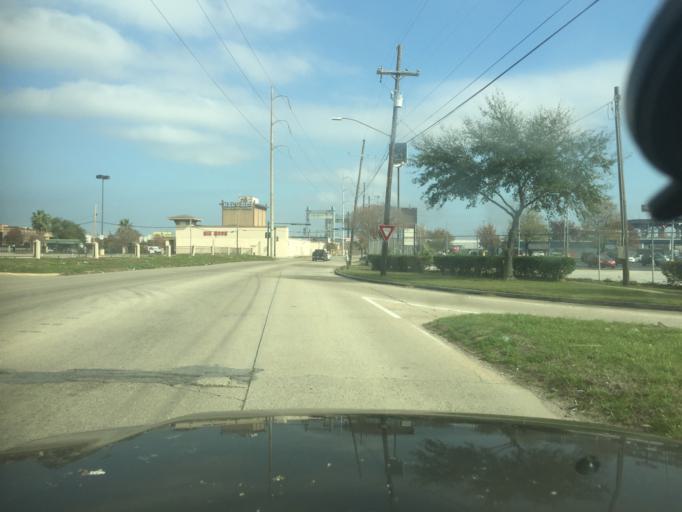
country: US
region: Louisiana
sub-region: Saint Bernard Parish
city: Arabi
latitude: 30.0045
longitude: -90.0346
